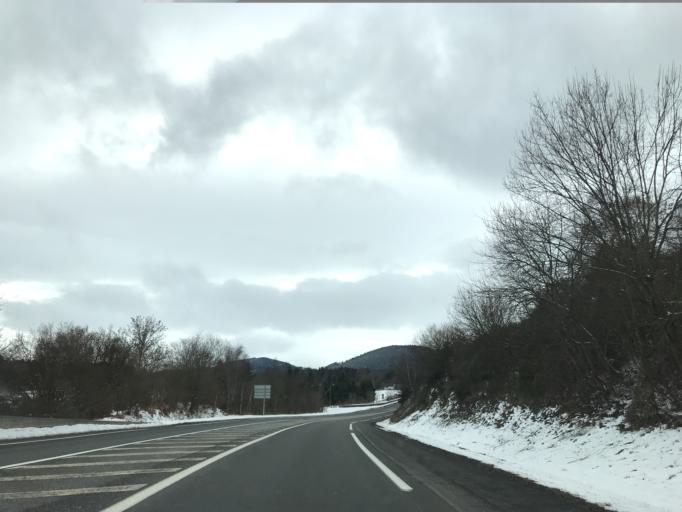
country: FR
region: Auvergne
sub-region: Departement du Puy-de-Dome
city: Saint-Genes-Champanelle
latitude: 45.6929
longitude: 2.9944
